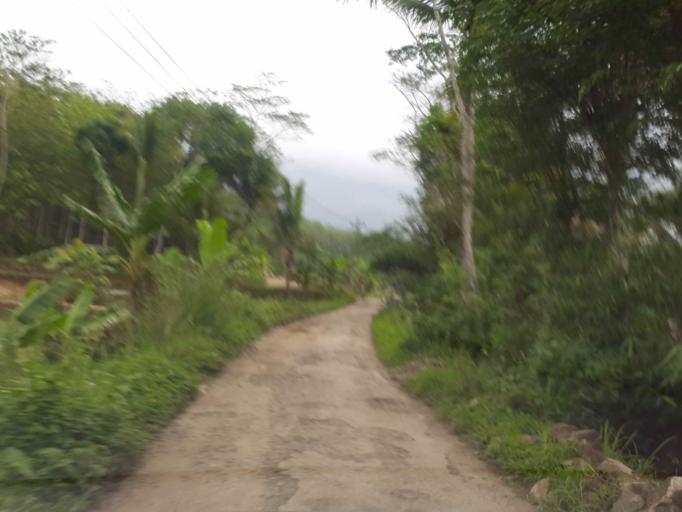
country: ID
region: Central Java
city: Pasanggrahan
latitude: -7.3678
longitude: 108.8964
